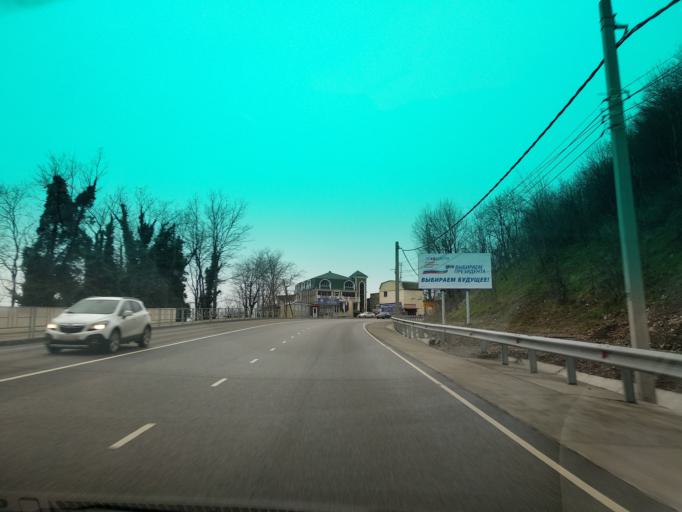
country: RU
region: Krasnodarskiy
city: Tuapse
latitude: 44.1059
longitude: 39.0778
